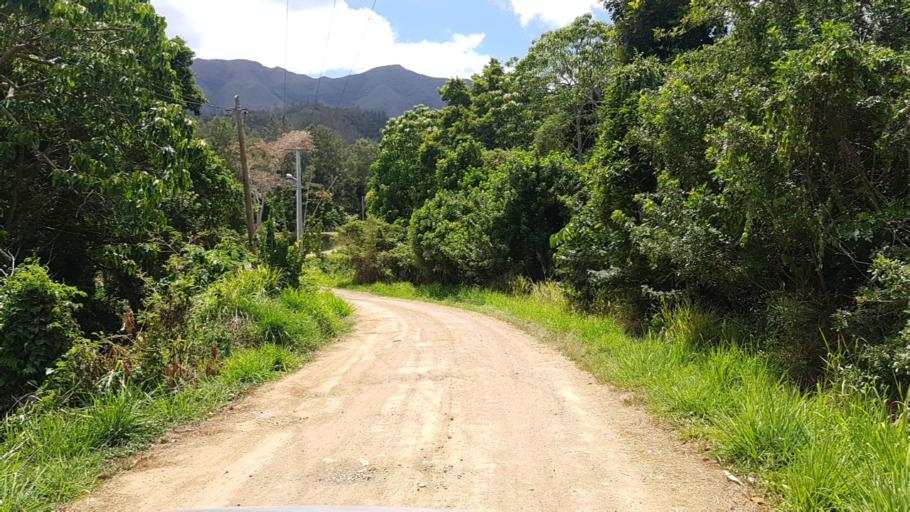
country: NC
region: South Province
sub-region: Dumbea
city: Dumbea
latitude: -22.1804
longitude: 166.4824
